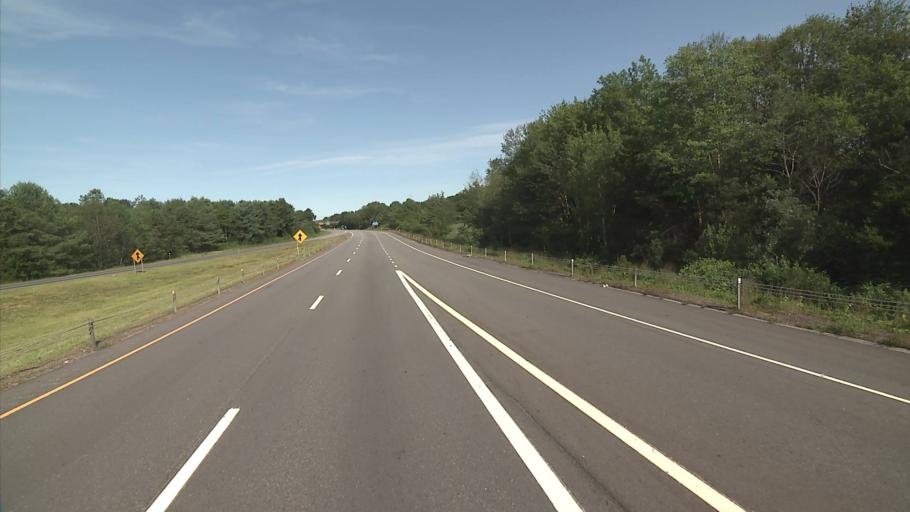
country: US
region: Connecticut
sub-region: New London County
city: Colchester
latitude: 41.5642
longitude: -72.3252
